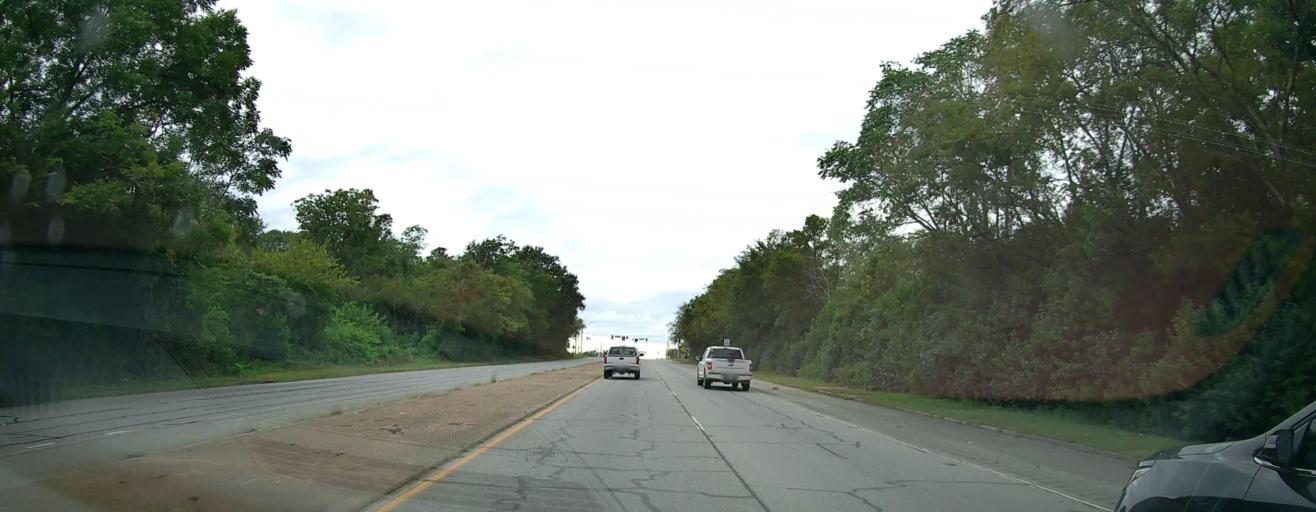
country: US
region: Georgia
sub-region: Bibb County
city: Macon
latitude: 32.8139
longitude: -83.6423
